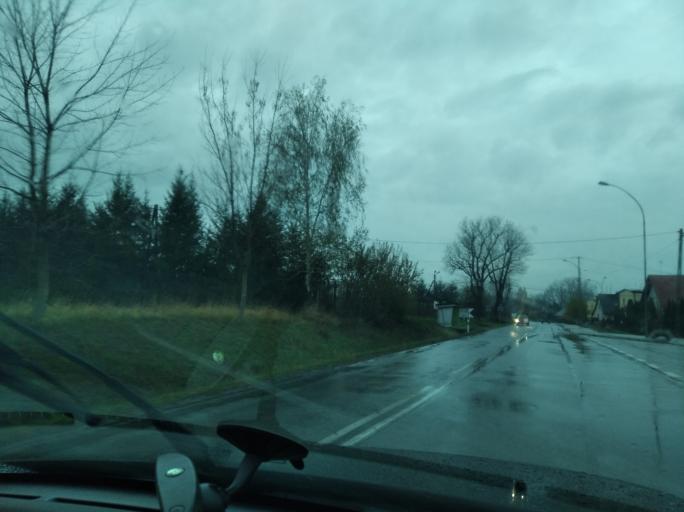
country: PL
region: Subcarpathian Voivodeship
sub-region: Powiat lancucki
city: Albigowa
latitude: 50.0289
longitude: 22.2276
